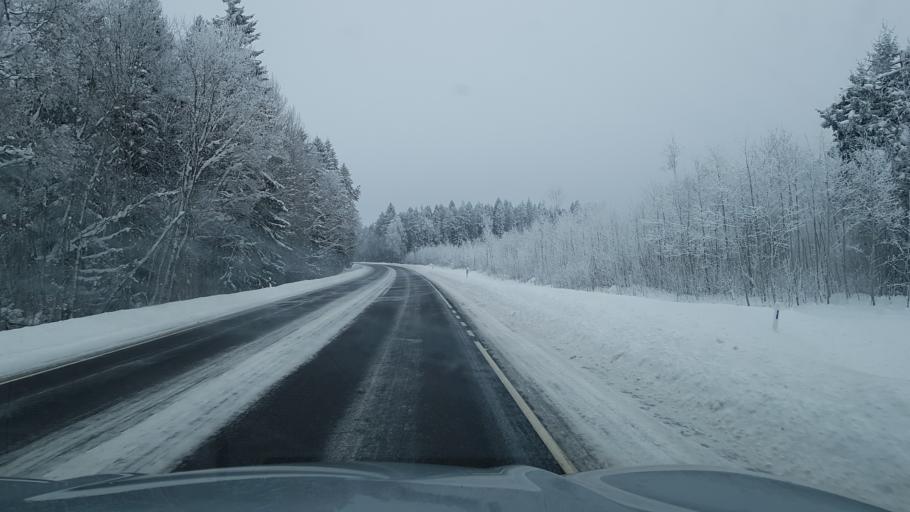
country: EE
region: Ida-Virumaa
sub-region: Johvi vald
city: Johvi
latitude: 59.2862
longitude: 27.3979
